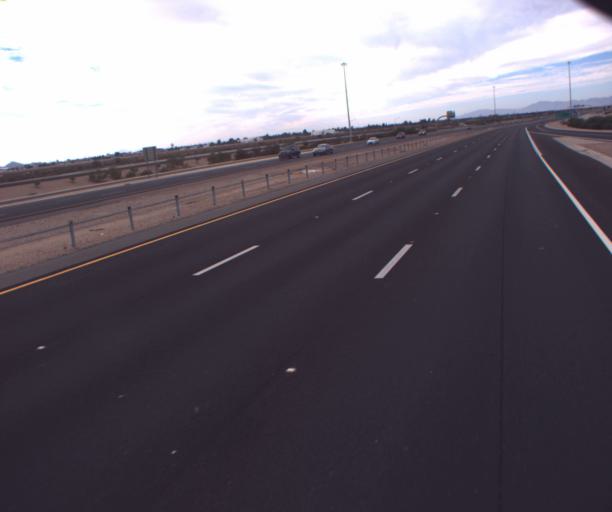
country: US
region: Arizona
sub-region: Maricopa County
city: Queen Creek
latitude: 33.3302
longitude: -111.6569
